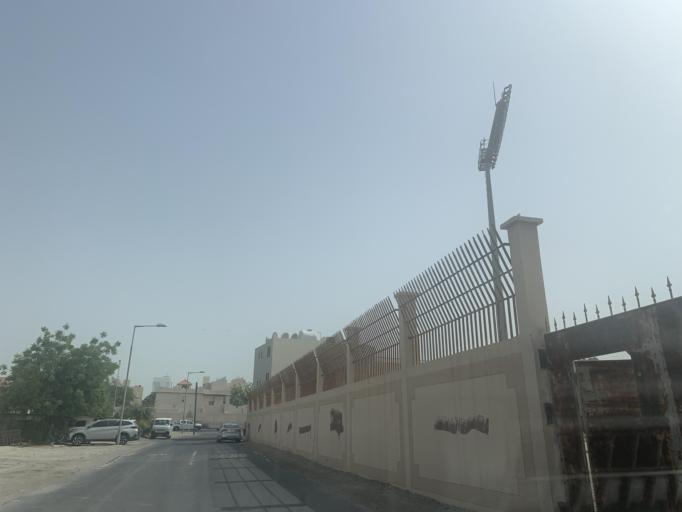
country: BH
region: Manama
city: Jidd Hafs
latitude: 26.2198
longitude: 50.5434
